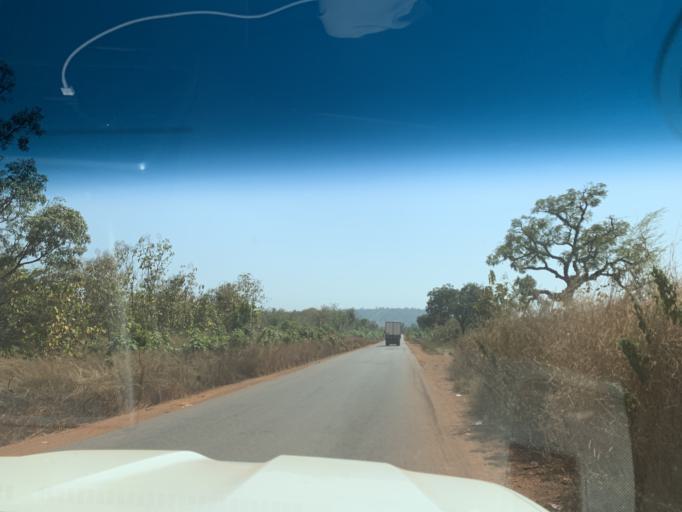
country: GN
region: Kindia
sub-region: Kindia
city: Kindia
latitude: 9.9945
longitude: -12.7519
